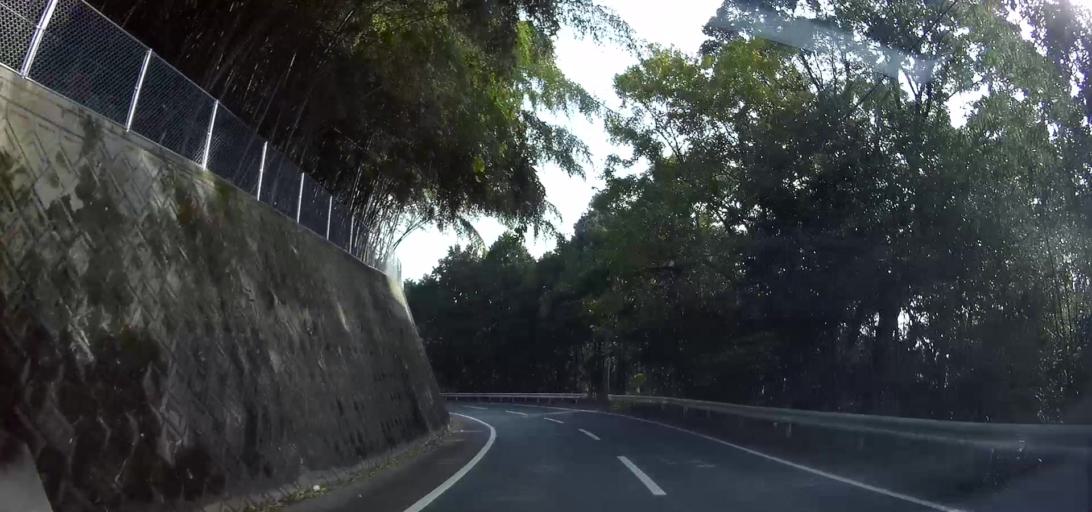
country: JP
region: Nagasaki
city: Shimabara
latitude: 32.6753
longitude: 130.2090
